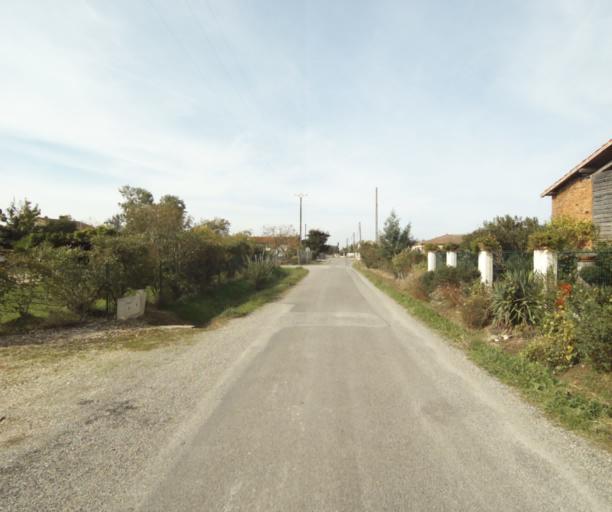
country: FR
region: Midi-Pyrenees
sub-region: Departement du Tarn-et-Garonne
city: Orgueil
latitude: 43.9074
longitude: 1.4069
